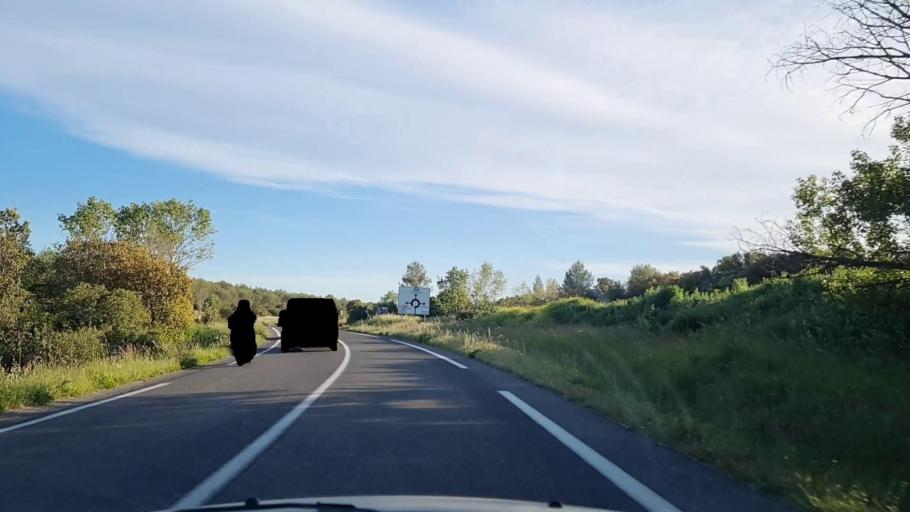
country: FR
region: Languedoc-Roussillon
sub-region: Departement du Gard
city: Villevieille
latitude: 43.8652
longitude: 4.0993
